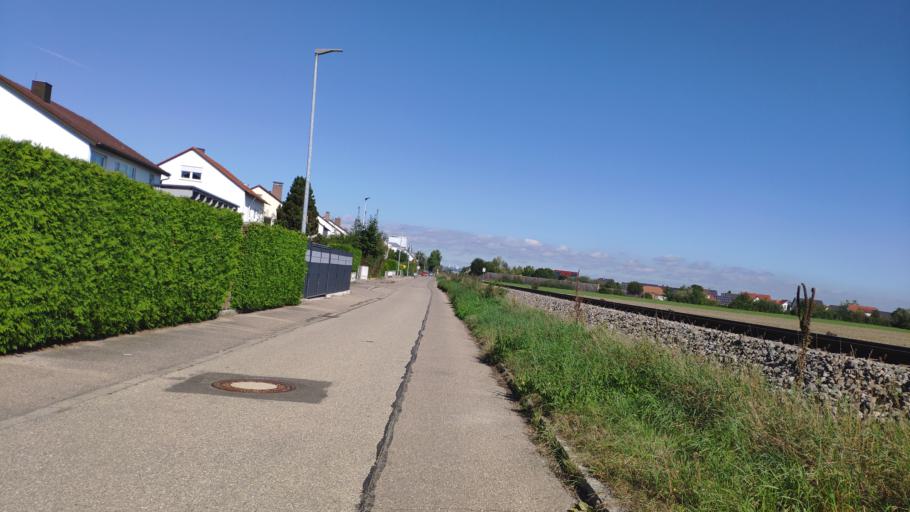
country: DE
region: Bavaria
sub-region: Swabia
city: Senden
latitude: 48.3461
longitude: 10.0386
